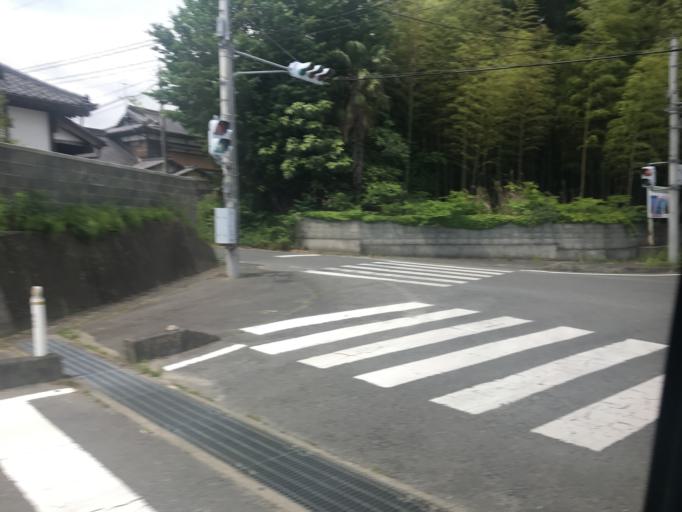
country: JP
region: Fukushima
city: Namie
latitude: 37.2838
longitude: 141.0011
